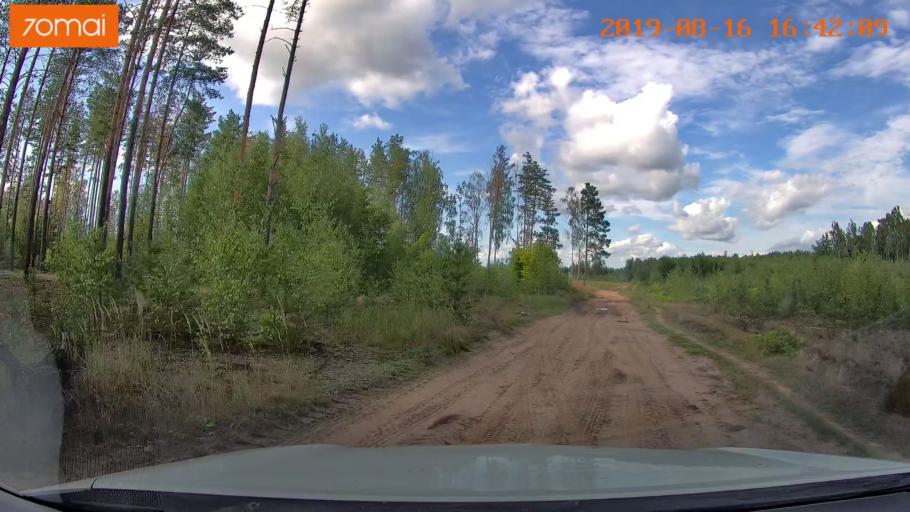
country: BY
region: Mogilev
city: Asipovichy
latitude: 53.2403
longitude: 28.7764
